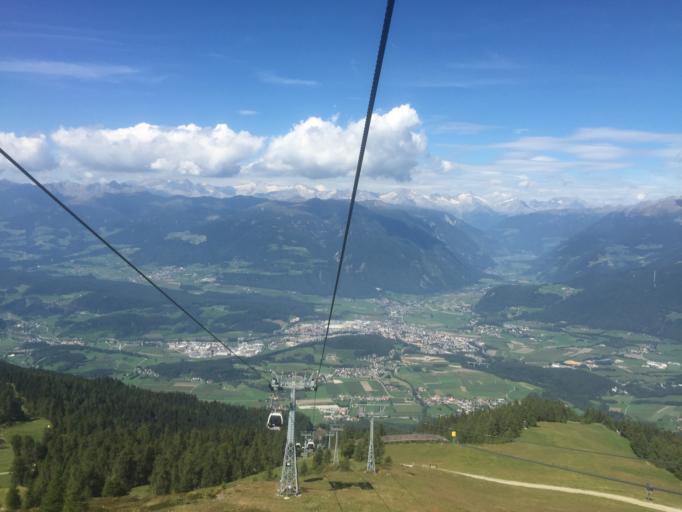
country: IT
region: Trentino-Alto Adige
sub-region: Bolzano
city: Riscone
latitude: 46.7421
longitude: 11.9559
